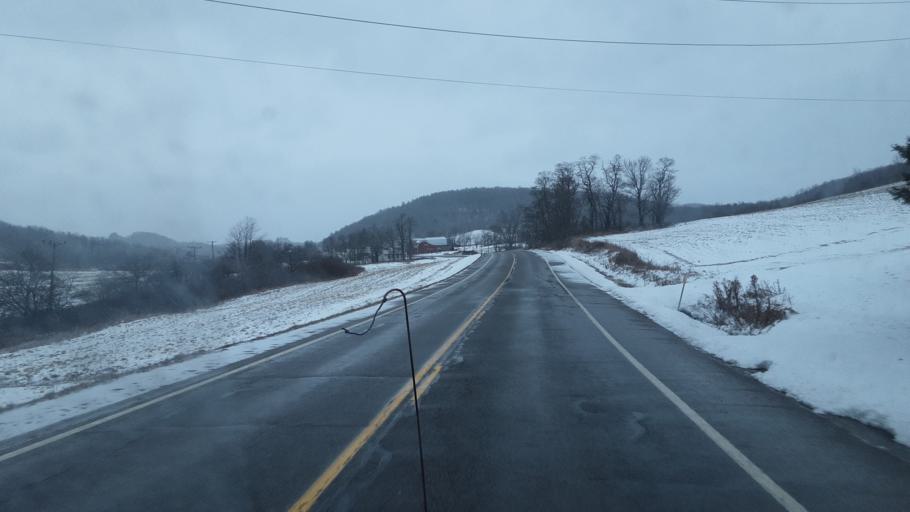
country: US
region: Pennsylvania
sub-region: Tioga County
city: Westfield
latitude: 42.0781
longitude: -77.5436
